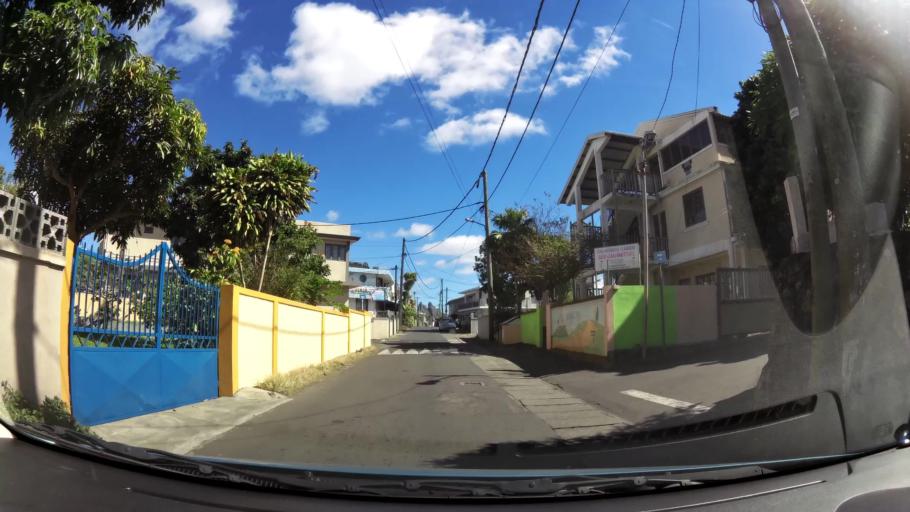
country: MU
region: Plaines Wilhems
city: Vacoas
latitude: -20.3060
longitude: 57.4837
